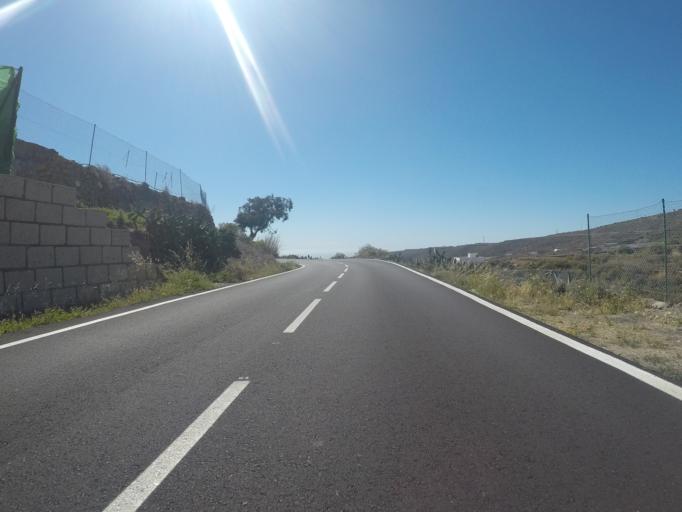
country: ES
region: Canary Islands
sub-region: Provincia de Santa Cruz de Tenerife
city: Lomo de Arico
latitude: 28.1718
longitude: -16.4980
